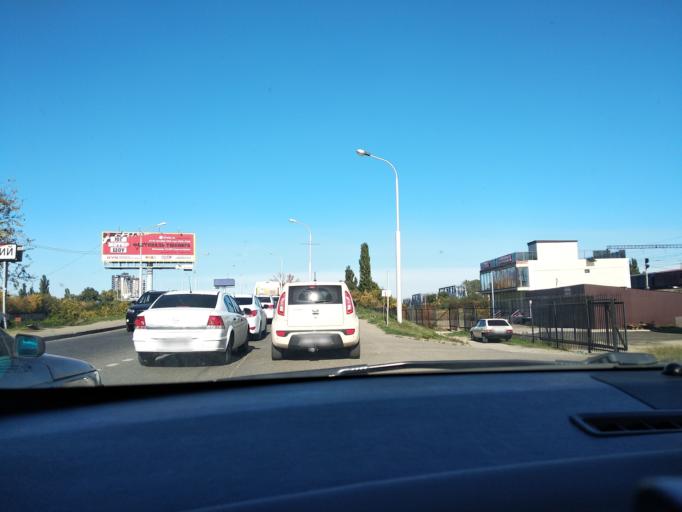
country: RU
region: Adygeya
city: Yablonovskiy
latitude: 44.9919
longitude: 38.9555
